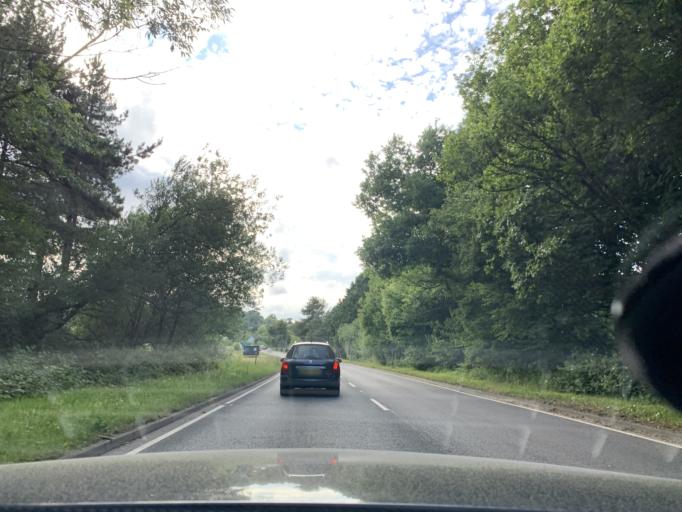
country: GB
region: England
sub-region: East Sussex
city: Robertsbridge
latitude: 50.9600
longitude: 0.4897
